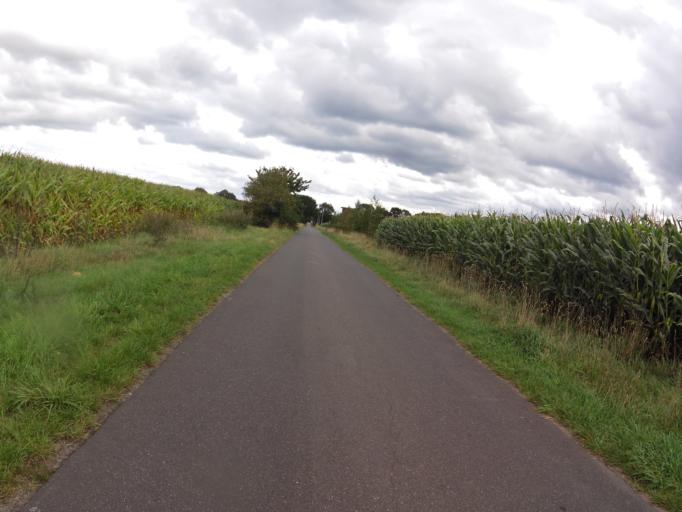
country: DE
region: Lower Saxony
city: Kohlen
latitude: 53.5113
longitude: 8.8568
